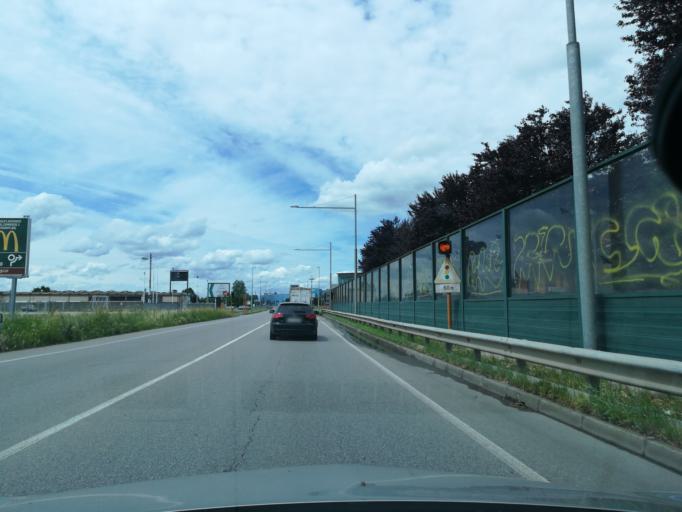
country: IT
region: Lombardy
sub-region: Provincia di Bergamo
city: Antegnate
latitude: 45.4812
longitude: 9.7882
